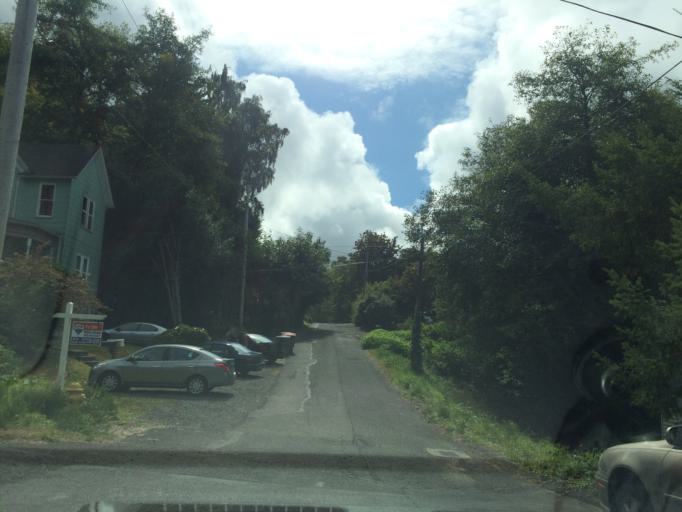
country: US
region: Oregon
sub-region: Clatsop County
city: Astoria
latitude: 46.1881
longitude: -123.8134
